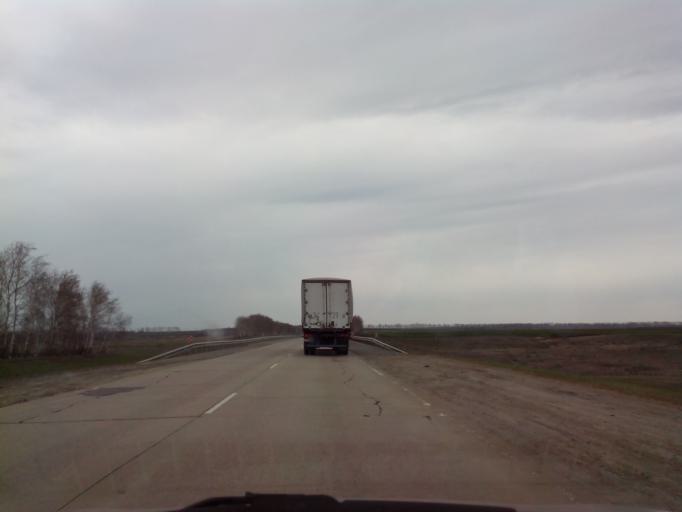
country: RU
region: Tambov
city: Pokrovo-Prigorodnoye
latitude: 52.6445
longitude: 41.3412
